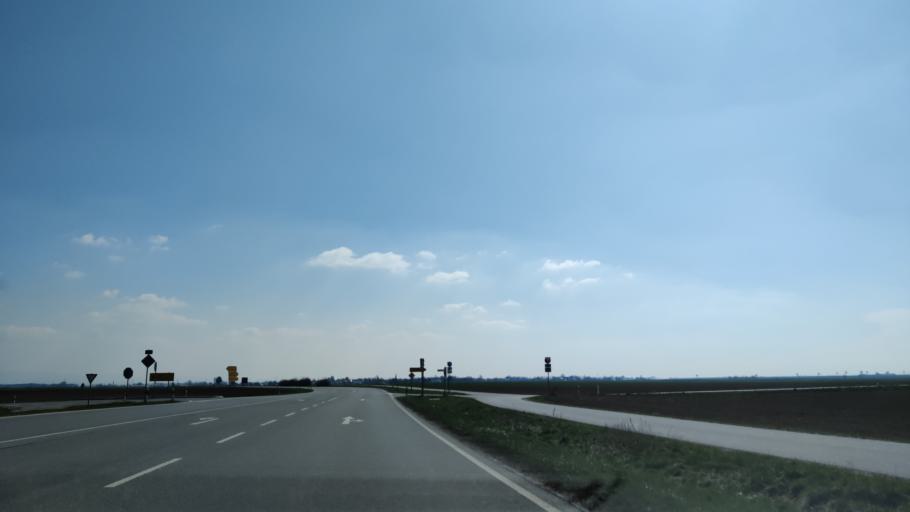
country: DE
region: Bavaria
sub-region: Lower Bavaria
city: Strasskirchen
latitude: 48.8394
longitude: 12.6827
